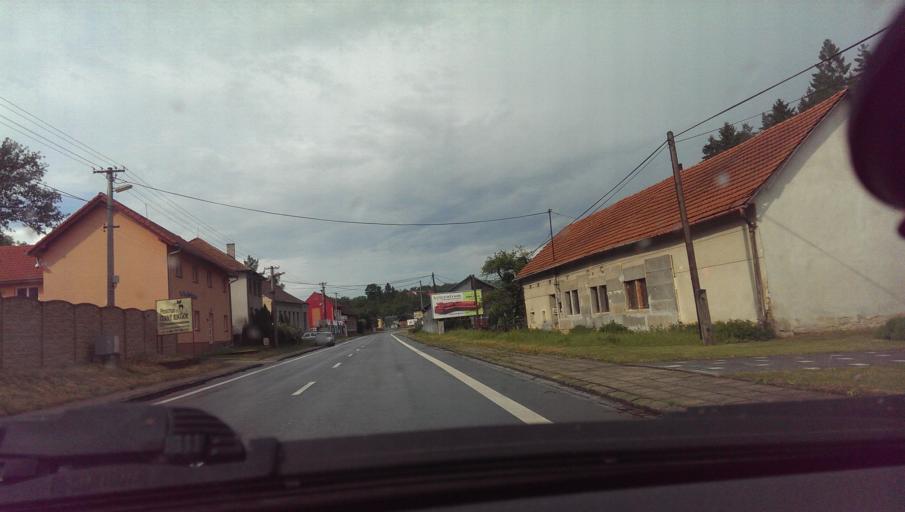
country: CZ
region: Zlin
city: Brezolupy
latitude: 49.1503
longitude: 17.6085
